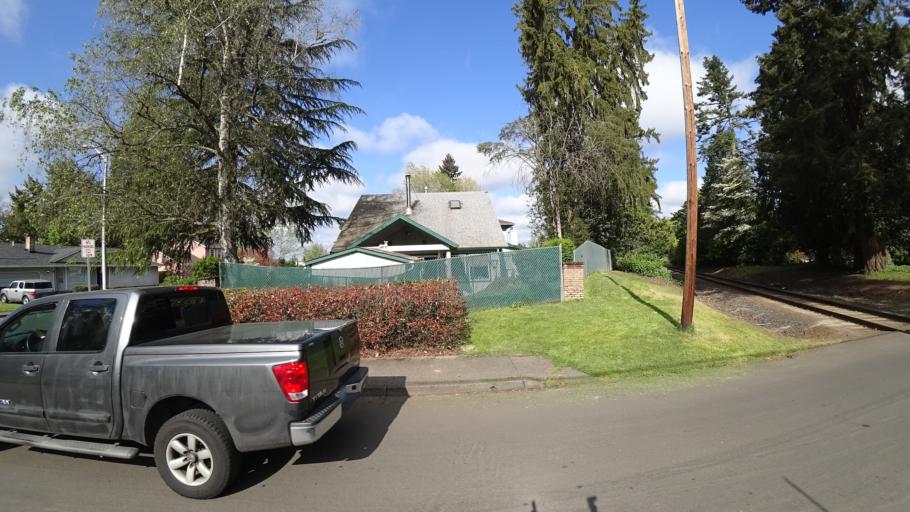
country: US
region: Oregon
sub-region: Washington County
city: Hillsboro
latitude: 45.5139
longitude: -122.9792
